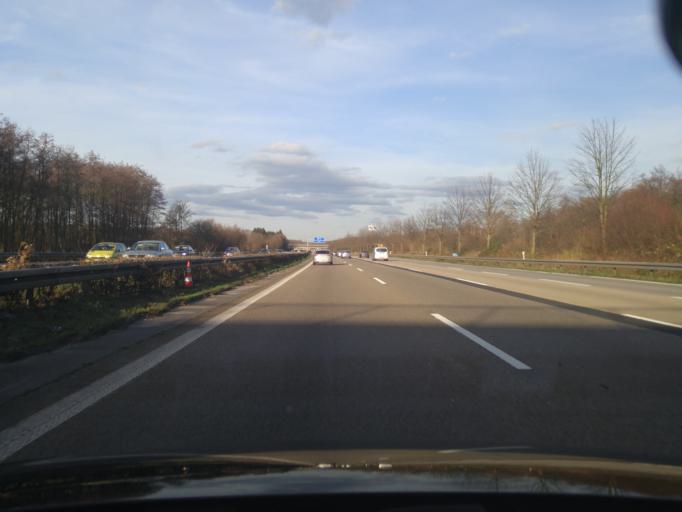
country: DE
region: North Rhine-Westphalia
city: Leichlingen
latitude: 51.0876
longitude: 6.9887
